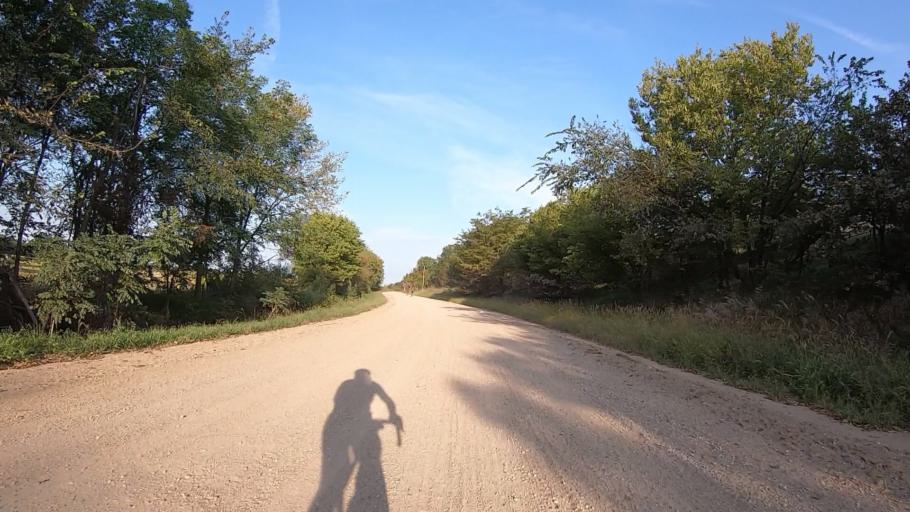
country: US
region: Kansas
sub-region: Marshall County
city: Blue Rapids
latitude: 39.7217
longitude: -96.7733
